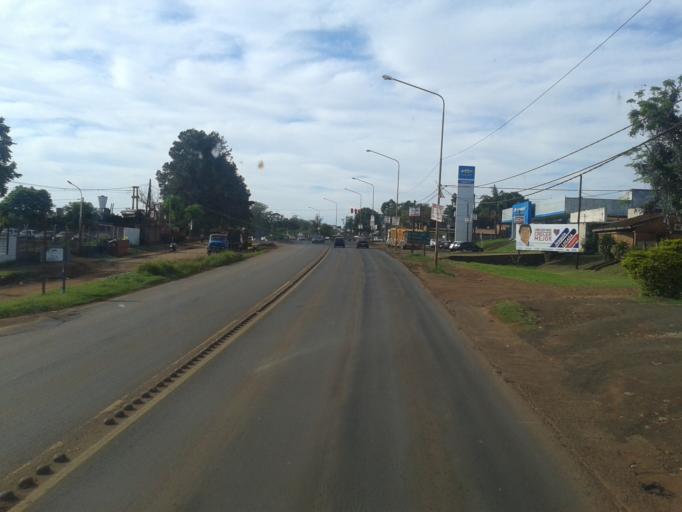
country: AR
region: Misiones
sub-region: Departamento de Capital
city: Posadas
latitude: -27.4228
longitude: -55.8988
